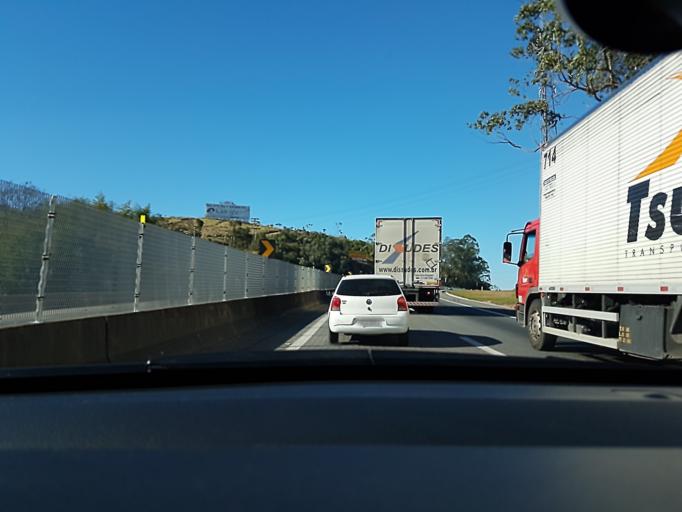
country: BR
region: Sao Paulo
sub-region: Aruja
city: Aruja
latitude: -23.3785
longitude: -46.2555
